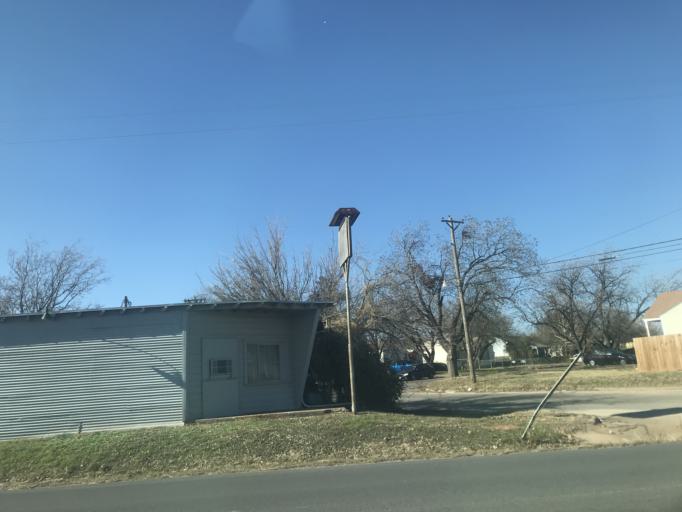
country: US
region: Texas
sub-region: Taylor County
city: Abilene
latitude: 32.4229
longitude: -99.7357
